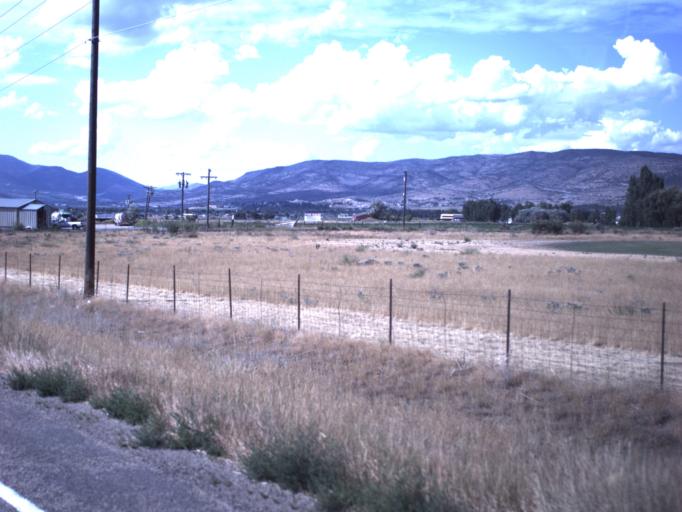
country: US
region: Utah
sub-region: Wasatch County
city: Heber
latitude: 40.4770
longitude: -111.3971
